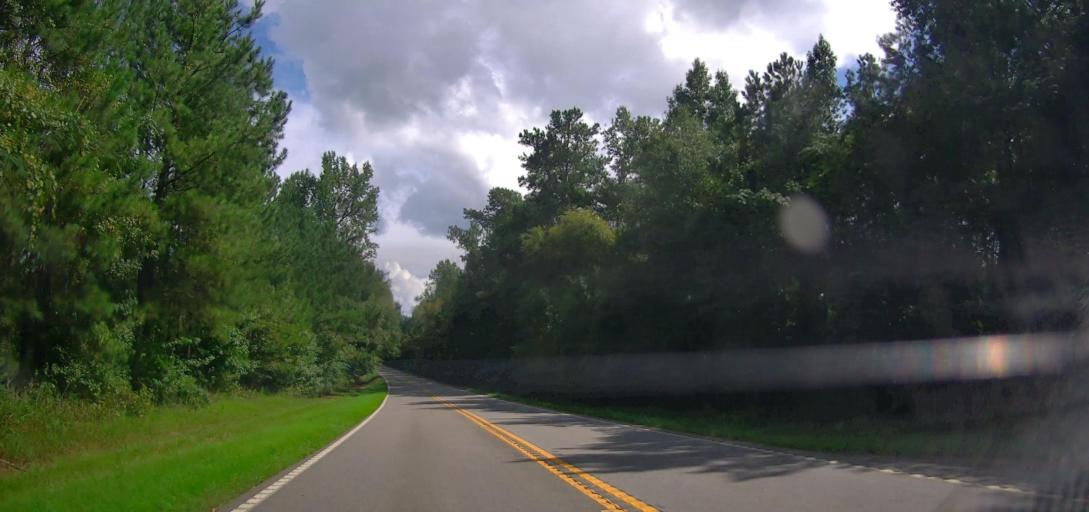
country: US
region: Georgia
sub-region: Talbot County
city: Talbotton
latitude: 32.6467
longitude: -84.5046
